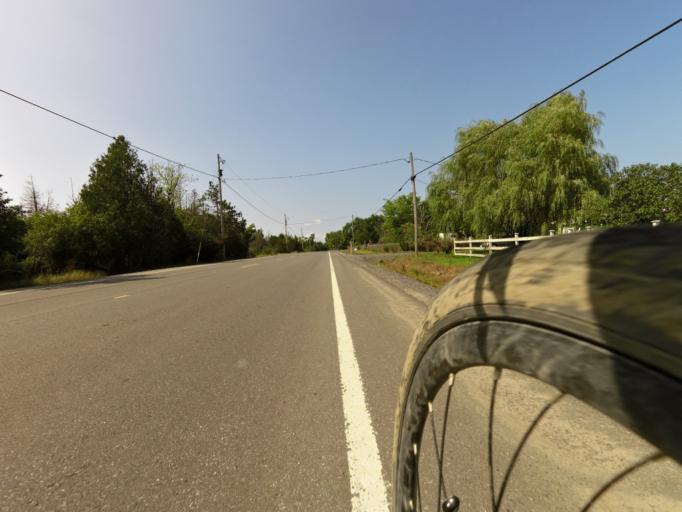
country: CA
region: Ontario
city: Skatepark
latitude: 44.2503
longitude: -76.7210
